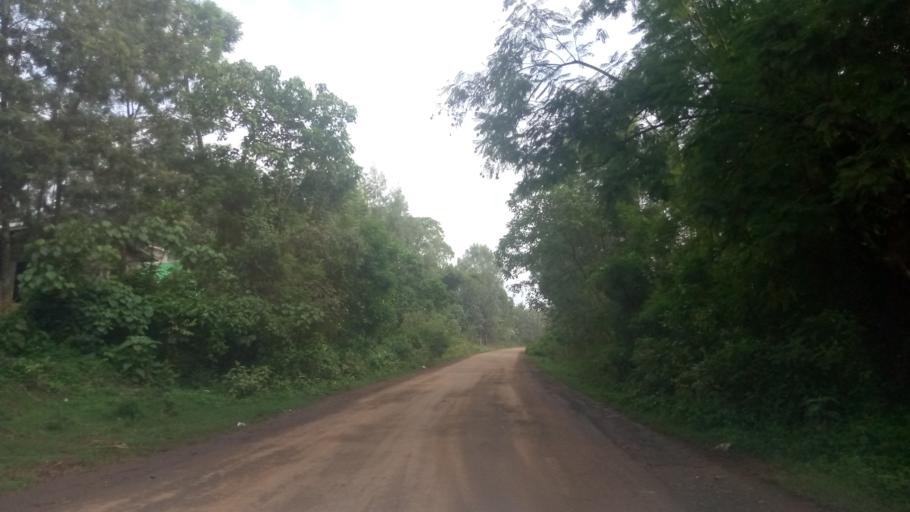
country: ET
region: Oromiya
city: Agaro
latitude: 7.8426
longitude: 36.6604
